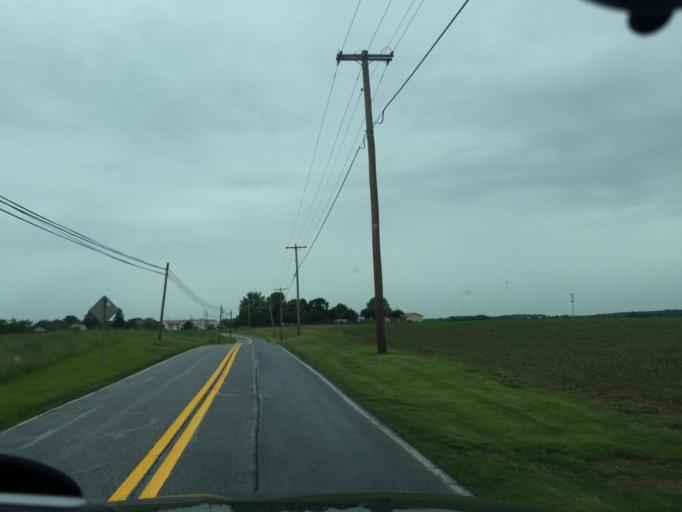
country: US
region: Maryland
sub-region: Carroll County
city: Taneytown
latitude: 39.5974
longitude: -77.2283
